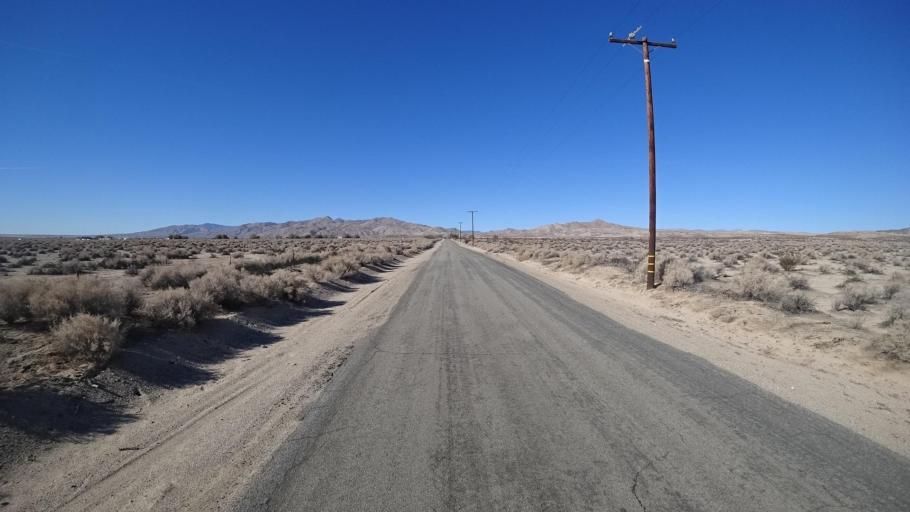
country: US
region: California
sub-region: Kern County
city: California City
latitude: 35.3089
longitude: -117.9622
